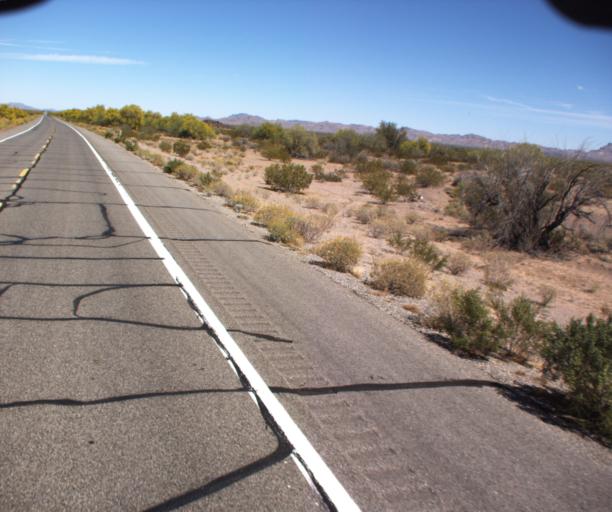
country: US
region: Arizona
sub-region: Pima County
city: Ajo
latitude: 32.5670
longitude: -112.8763
